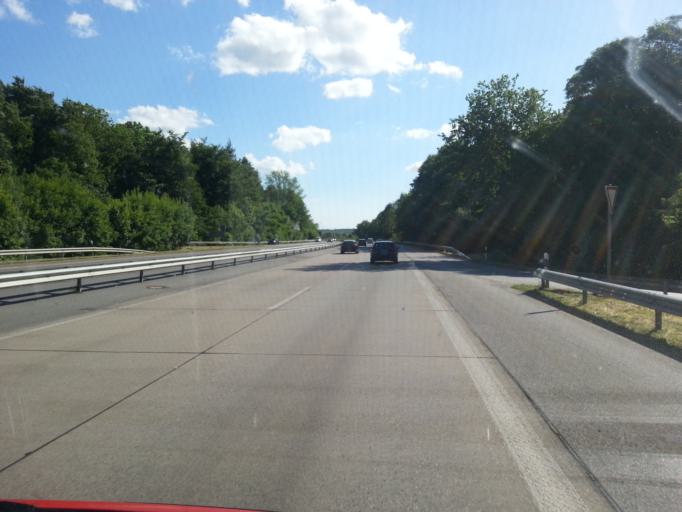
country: DE
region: Schleswig-Holstein
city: Susel
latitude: 54.0541
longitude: 10.7356
